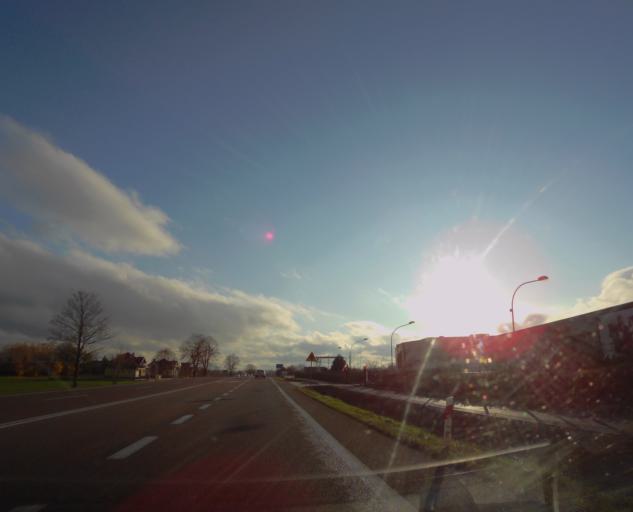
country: PL
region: Subcarpathian Voivodeship
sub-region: Powiat przemyski
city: Orly
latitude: 49.8474
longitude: 22.8031
